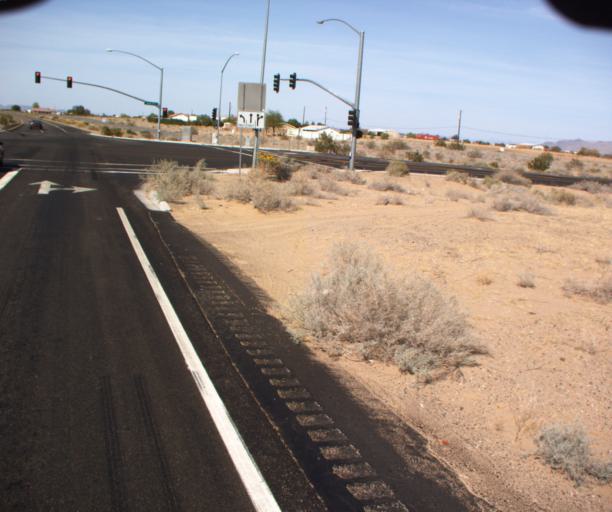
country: US
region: Arizona
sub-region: Yuma County
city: Fortuna Foothills
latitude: 32.6260
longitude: -114.5198
